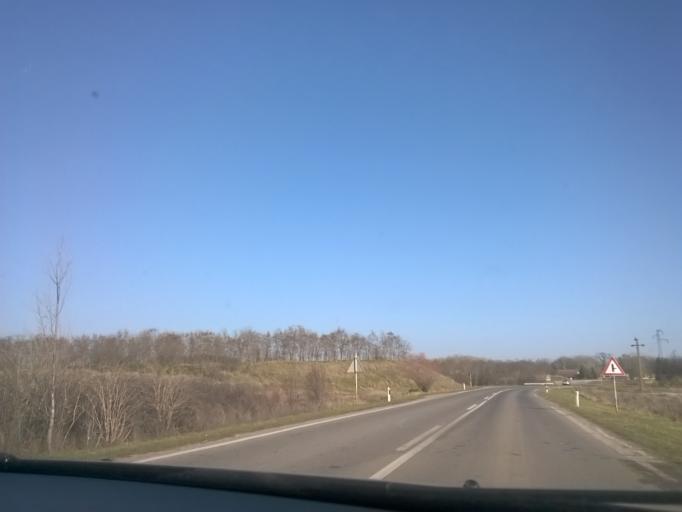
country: RS
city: Vlajkovac
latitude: 45.0683
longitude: 21.1915
